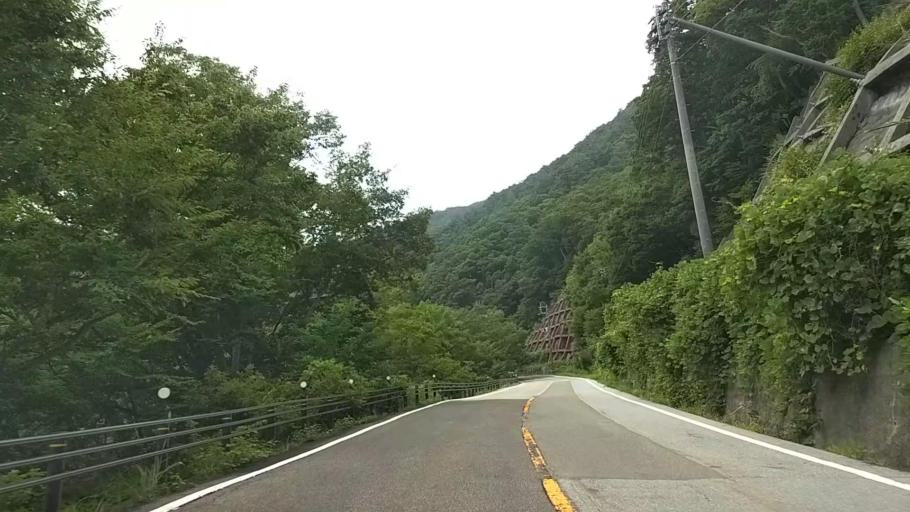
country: JP
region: Yamanashi
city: Fujikawaguchiko
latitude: 35.4748
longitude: 138.5787
